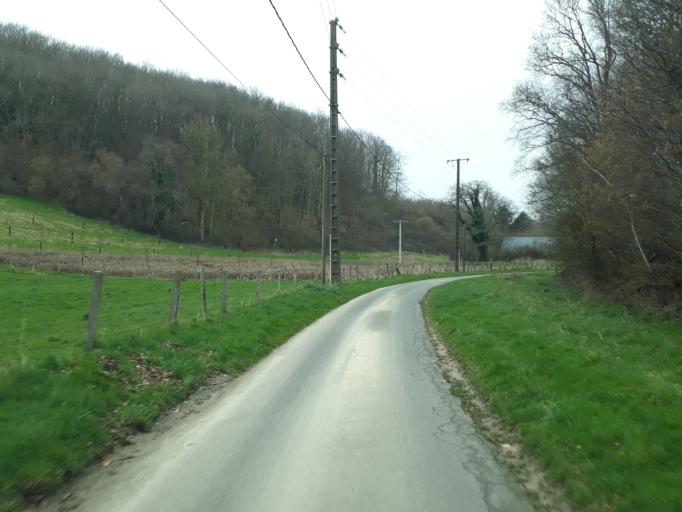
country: FR
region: Haute-Normandie
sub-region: Departement de la Seine-Maritime
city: Les Loges
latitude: 49.6723
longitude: 0.2669
